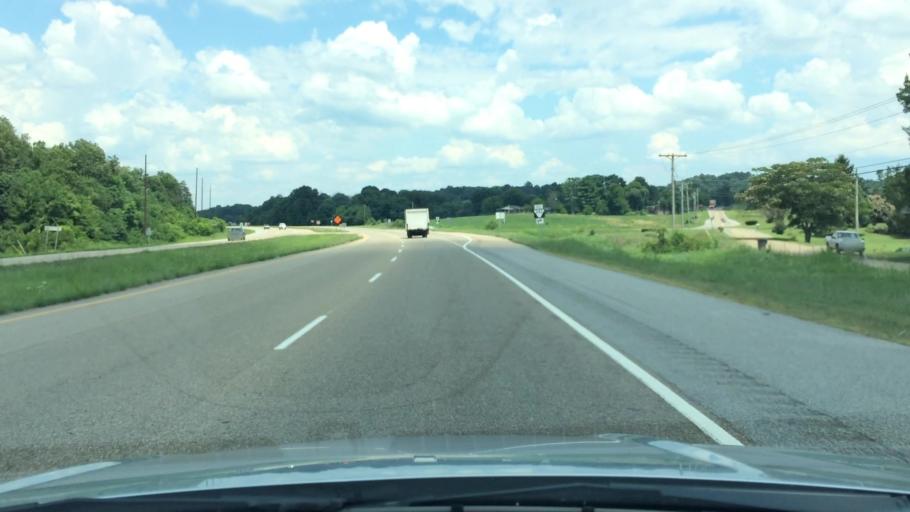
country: US
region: Tennessee
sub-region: Hamblen County
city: Morristown
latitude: 36.1657
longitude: -83.3690
